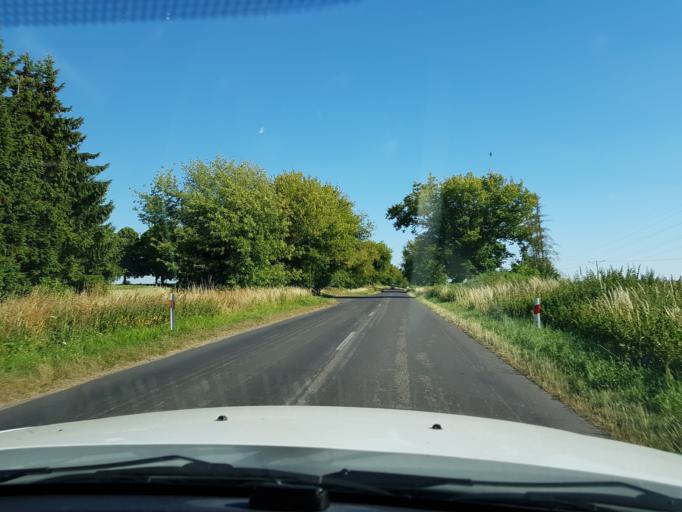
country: PL
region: West Pomeranian Voivodeship
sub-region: Powiat lobeski
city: Lobez
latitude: 53.6675
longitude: 15.6081
